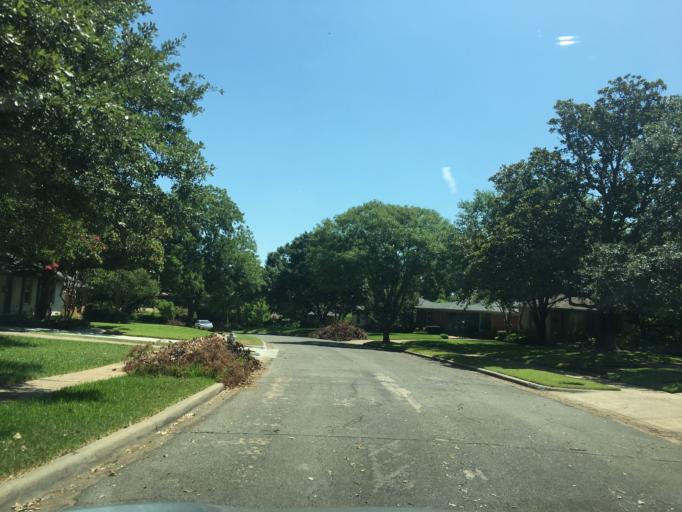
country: US
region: Texas
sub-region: Dallas County
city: Highland Park
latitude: 32.8393
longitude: -96.7506
